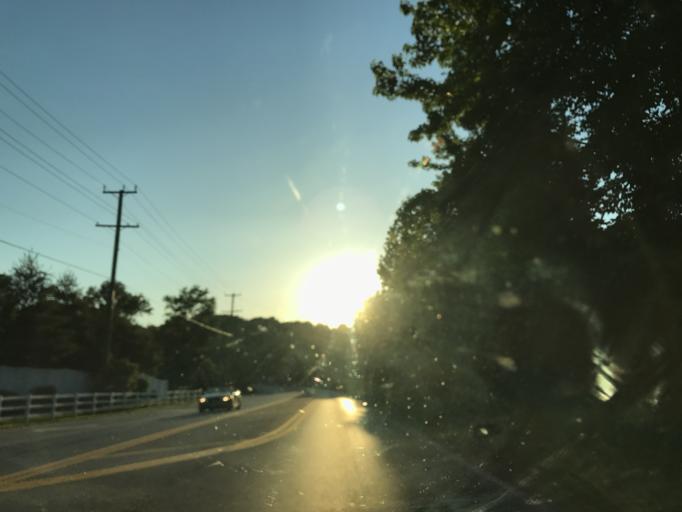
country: US
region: Maryland
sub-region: Anne Arundel County
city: Selby-on-the-Bay
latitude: 38.9059
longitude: -76.5251
